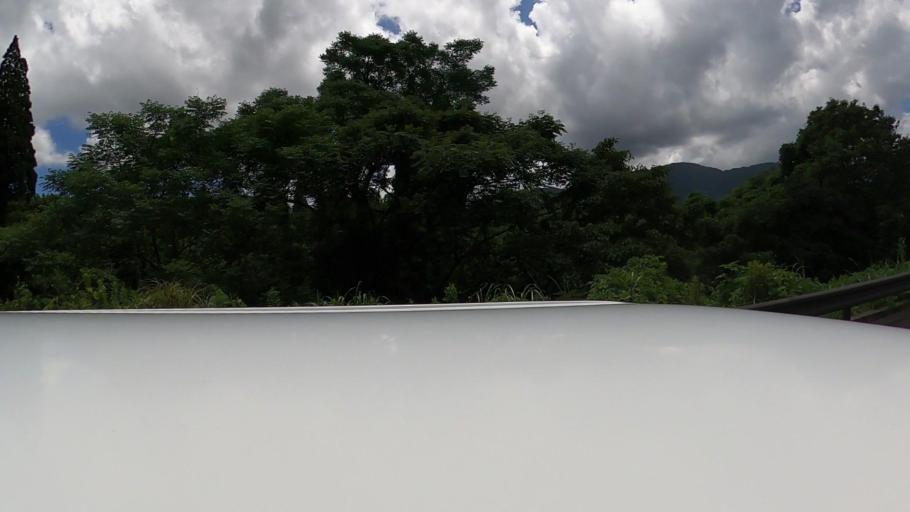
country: JP
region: Miyazaki
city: Nobeoka
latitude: 32.5859
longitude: 131.5122
